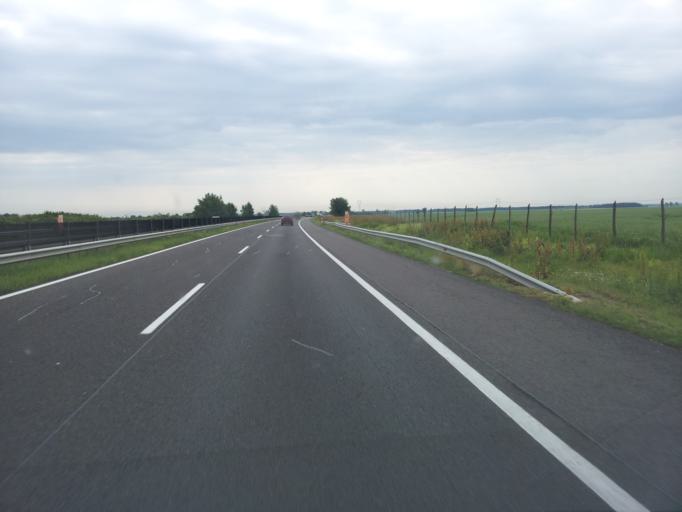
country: HU
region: Heves
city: Adacs
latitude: 47.7258
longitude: 19.9826
